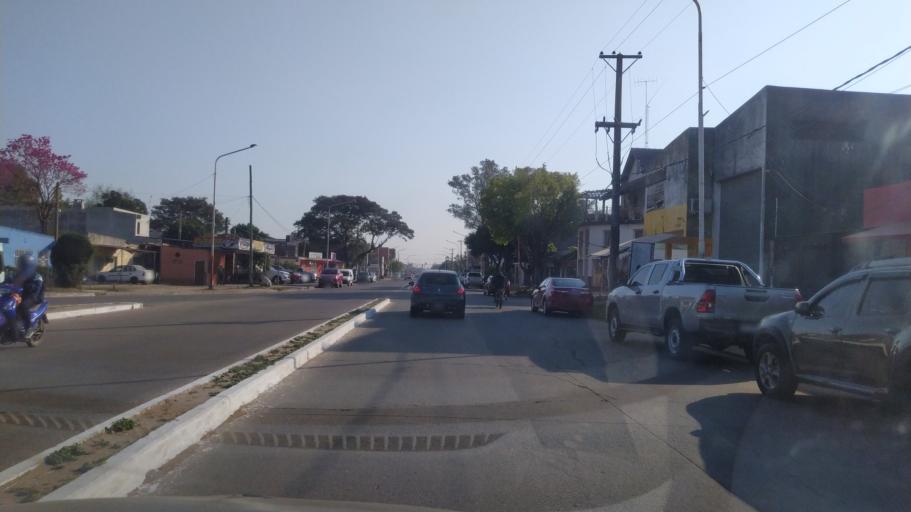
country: AR
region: Corrientes
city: Corrientes
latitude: -27.4893
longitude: -58.8167
